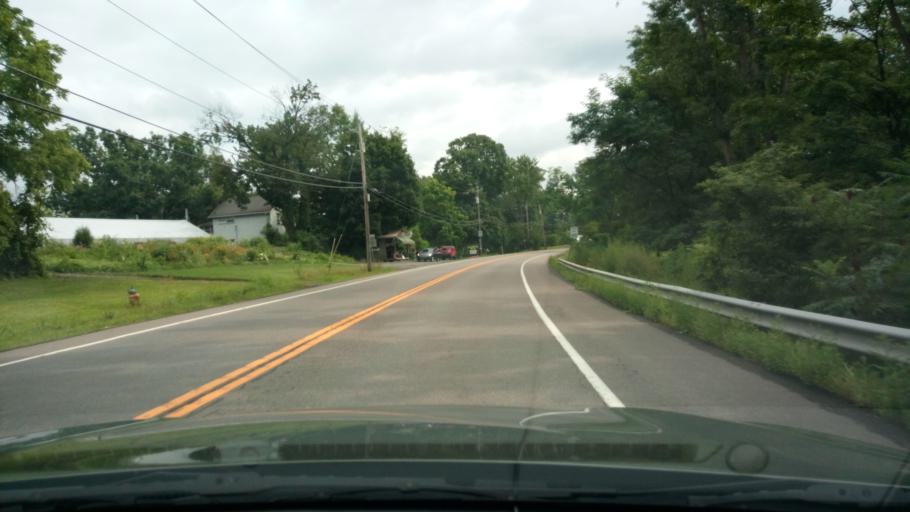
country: US
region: New York
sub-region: Tompkins County
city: South Hill
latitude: 42.4061
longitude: -76.5452
